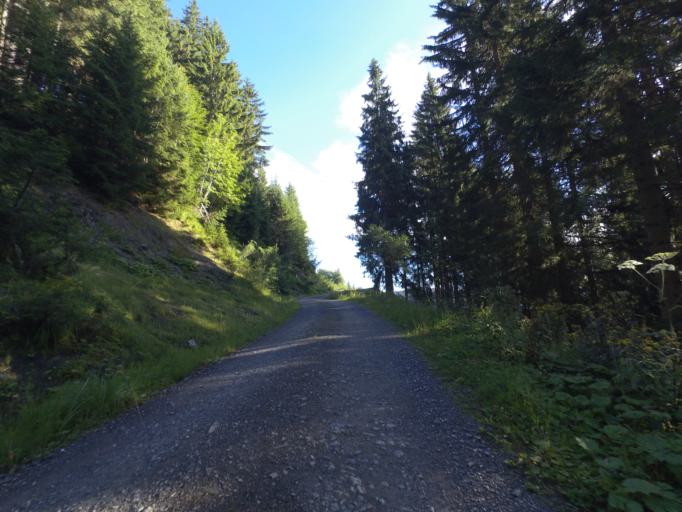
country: AT
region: Salzburg
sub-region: Politischer Bezirk Sankt Johann im Pongau
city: Goldegg
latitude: 47.3481
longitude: 13.1058
